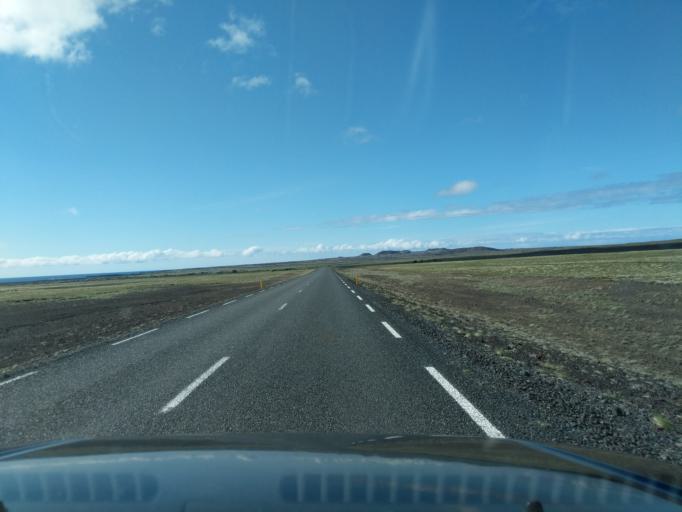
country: IS
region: West
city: Olafsvik
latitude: 64.8028
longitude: -23.9310
